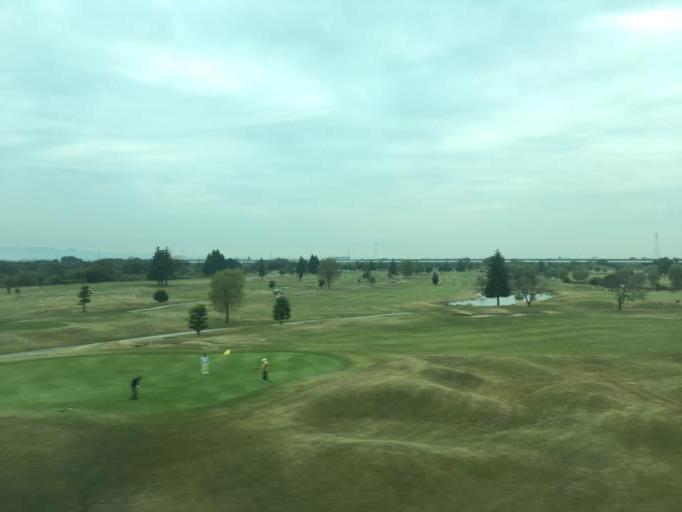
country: JP
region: Saitama
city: Kamifukuoka
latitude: 35.9081
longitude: 139.5511
